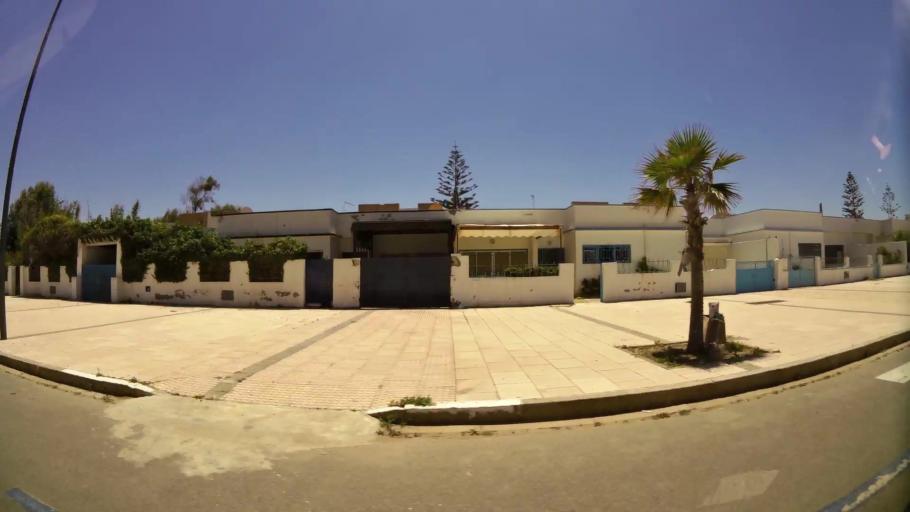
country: MA
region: Oriental
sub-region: Berkane-Taourirt
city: Madagh
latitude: 35.0877
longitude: -2.2308
